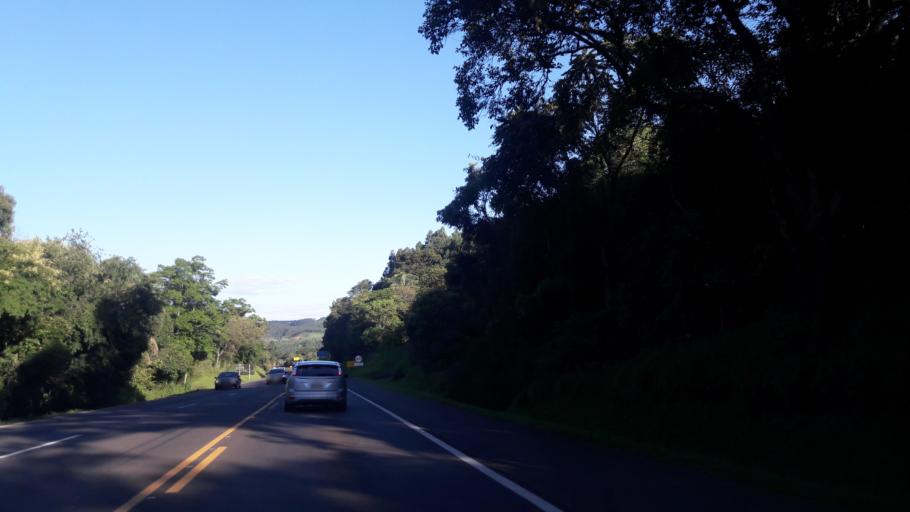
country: BR
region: Parana
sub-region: Prudentopolis
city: Prudentopolis
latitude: -25.3125
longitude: -51.1810
